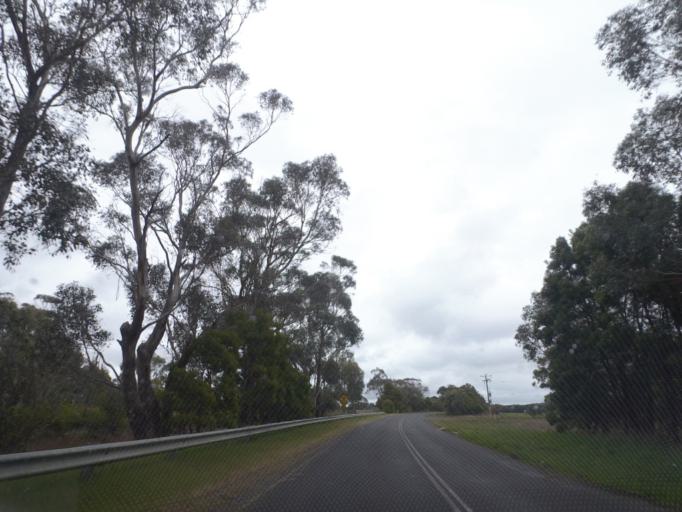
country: AU
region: Victoria
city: Brown Hill
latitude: -37.5961
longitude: 144.1580
